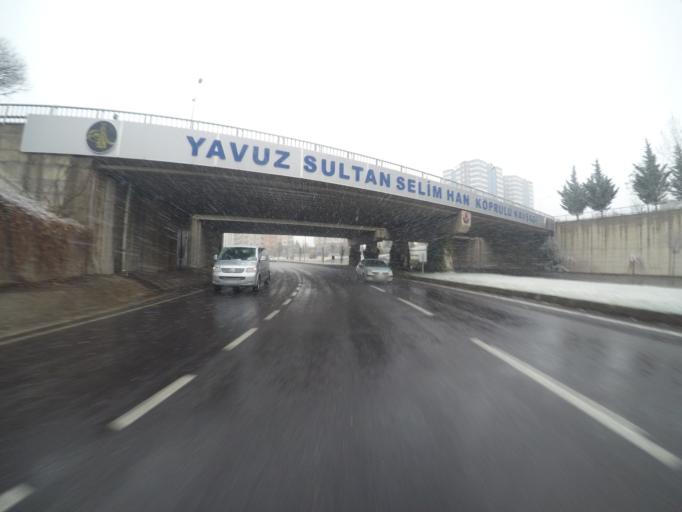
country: TR
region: Nevsehir
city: Nevsehir
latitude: 38.6302
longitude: 34.7288
